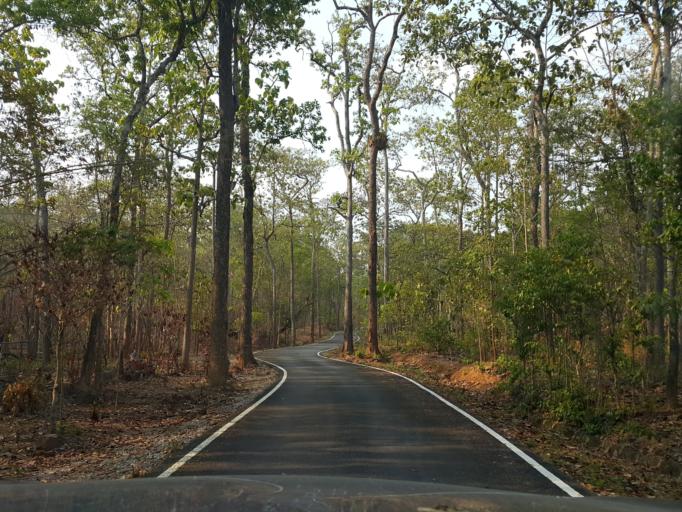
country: TH
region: Lamphun
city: Li
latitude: 17.6269
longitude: 98.8715
